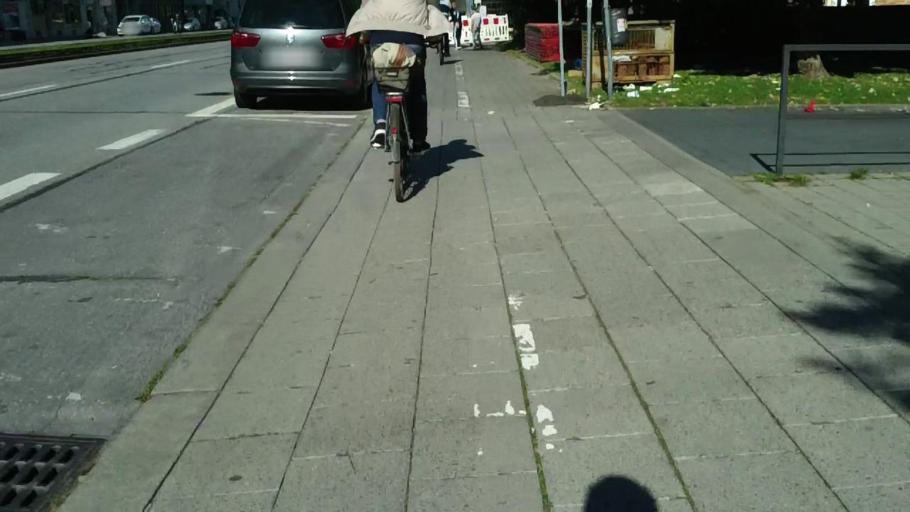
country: DE
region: Bavaria
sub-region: Upper Bavaria
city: Munich
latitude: 48.1524
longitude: 11.5563
